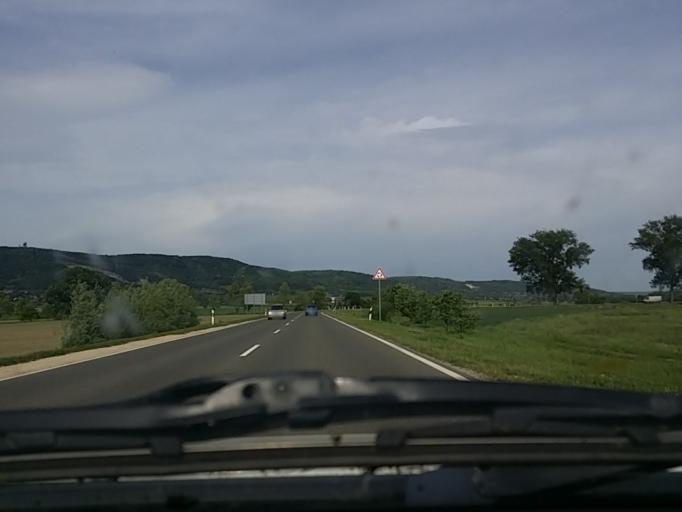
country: HU
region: Baranya
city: Harkany
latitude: 45.8632
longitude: 18.2304
